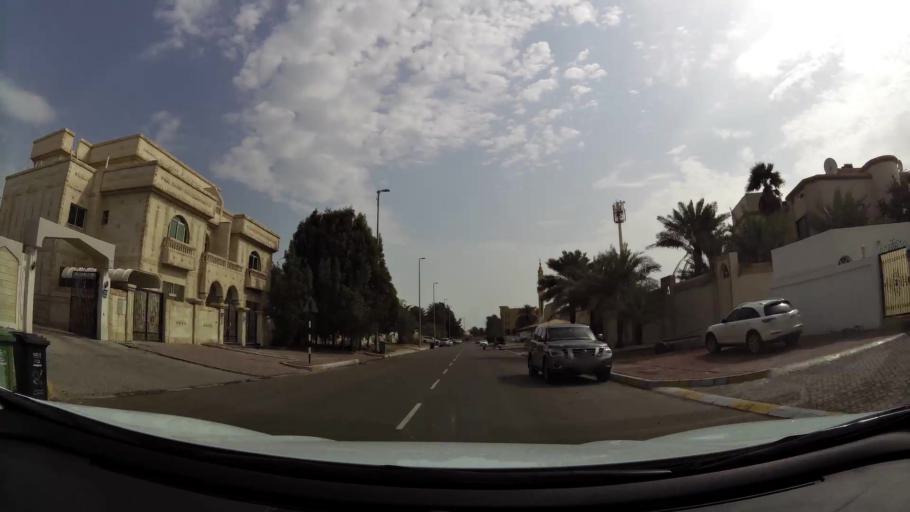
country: AE
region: Abu Dhabi
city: Abu Dhabi
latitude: 24.4432
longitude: 54.4292
